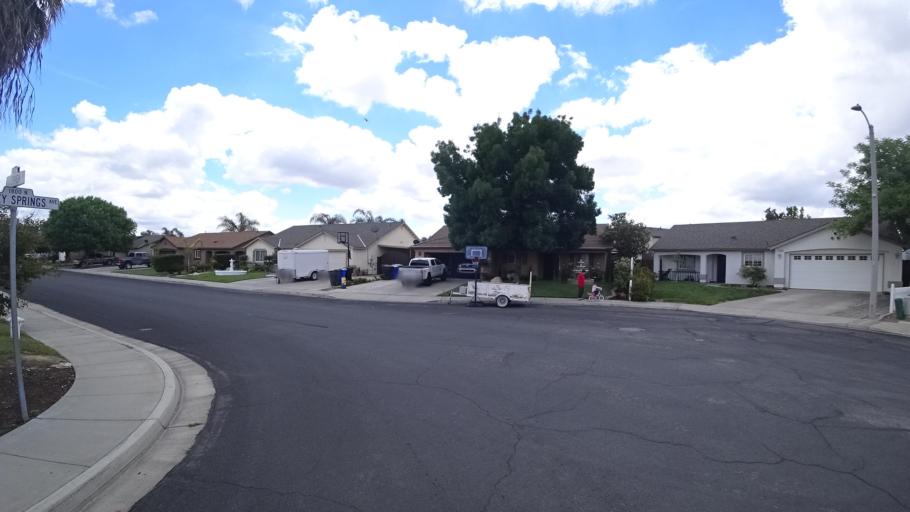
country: US
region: California
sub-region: Kings County
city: Hanford
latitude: 36.3454
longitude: -119.6275
